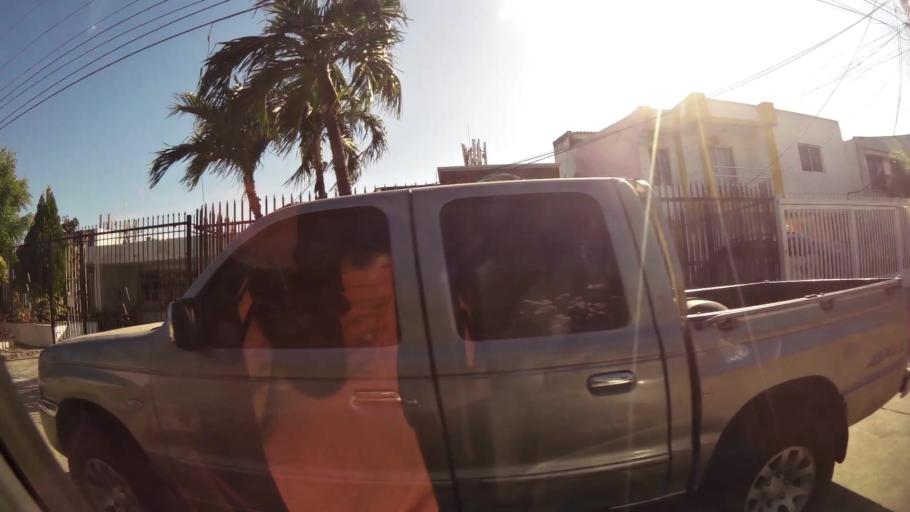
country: CO
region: Atlantico
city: Barranquilla
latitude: 10.9928
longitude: -74.8284
